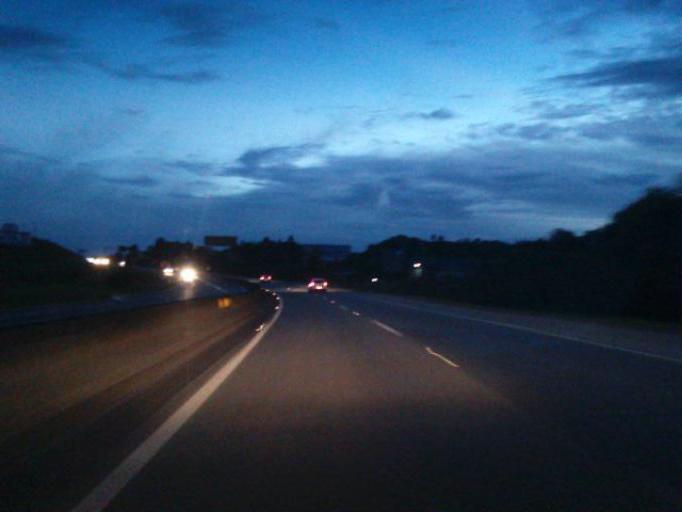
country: BR
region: Santa Catarina
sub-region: Barra Velha
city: Barra Velha
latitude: -26.6023
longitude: -48.7255
